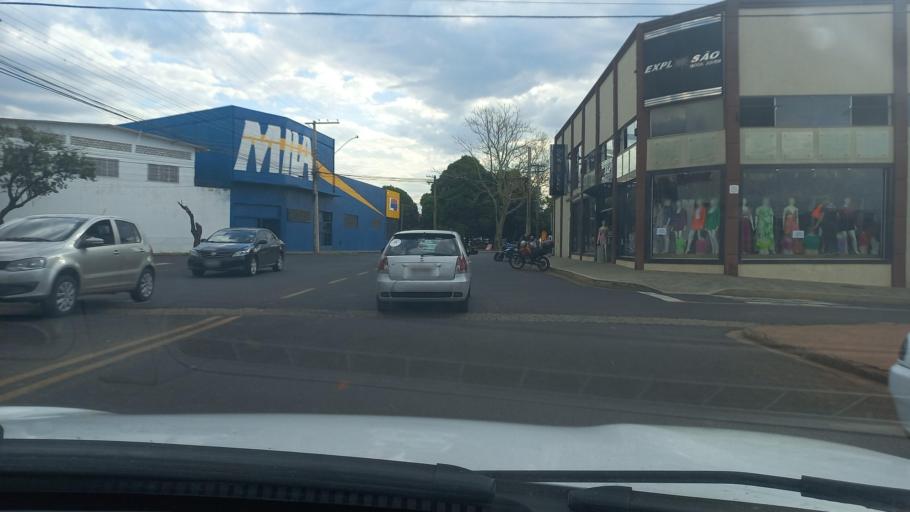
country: BR
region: Minas Gerais
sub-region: Uberaba
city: Uberaba
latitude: -19.7710
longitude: -47.9384
